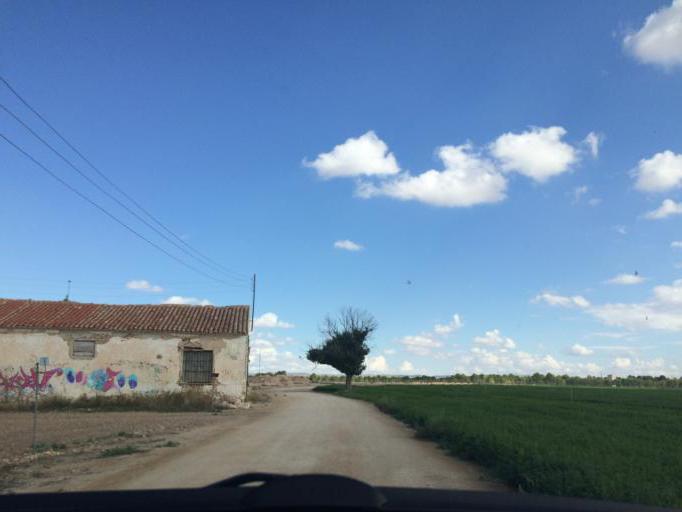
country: ES
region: Castille-La Mancha
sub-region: Provincia de Albacete
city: Albacete
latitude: 38.9588
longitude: -1.8616
